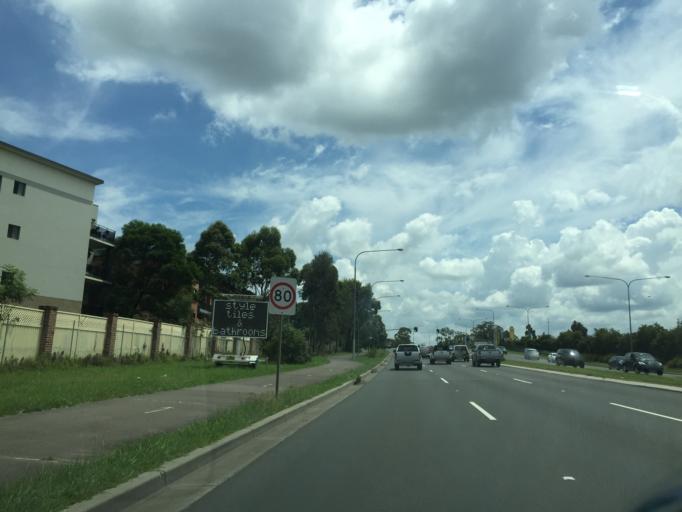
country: AU
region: New South Wales
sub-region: The Hills Shire
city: Beaumont Hills
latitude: -33.6987
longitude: 150.9281
